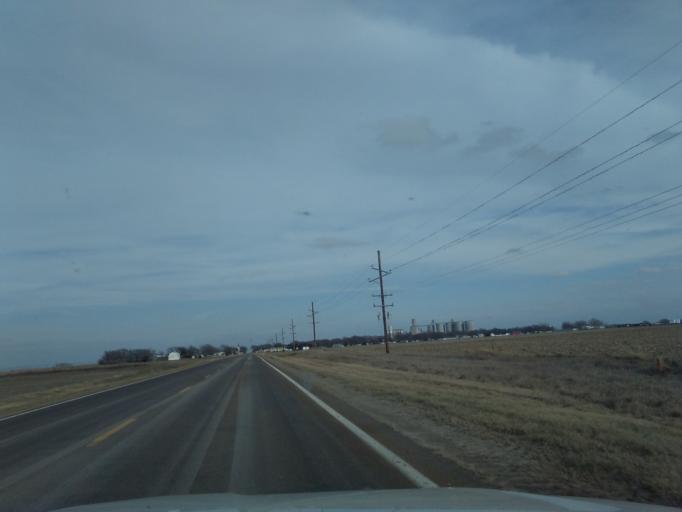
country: US
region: Nebraska
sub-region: Saline County
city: Wilber
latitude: 40.3061
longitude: -97.0076
